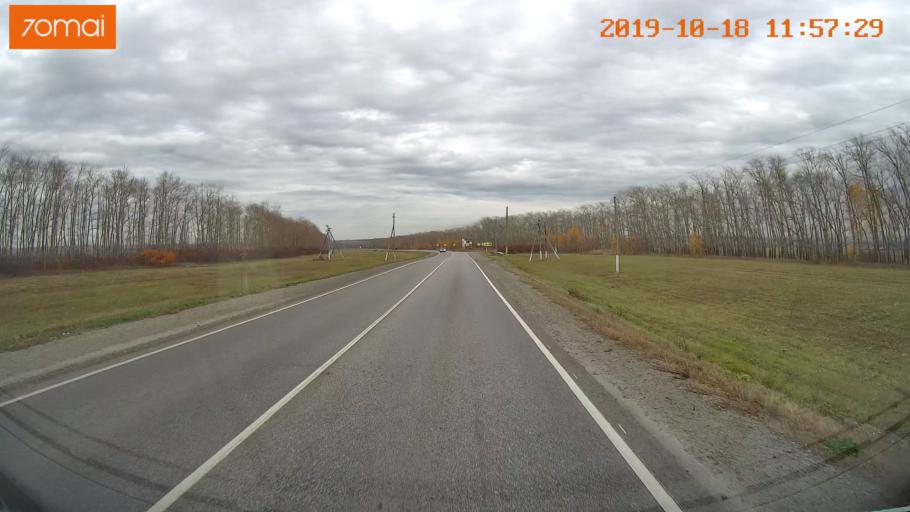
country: RU
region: Rjazan
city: Mikhaylov
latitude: 54.2664
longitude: 39.1452
